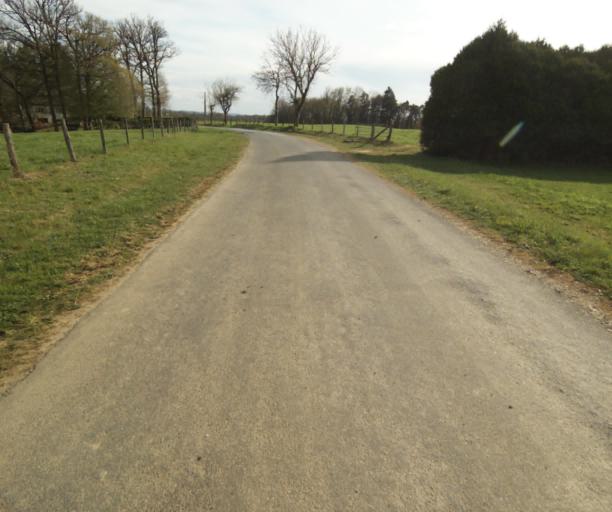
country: FR
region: Limousin
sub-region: Departement de la Correze
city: Naves
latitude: 45.3195
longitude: 1.7466
